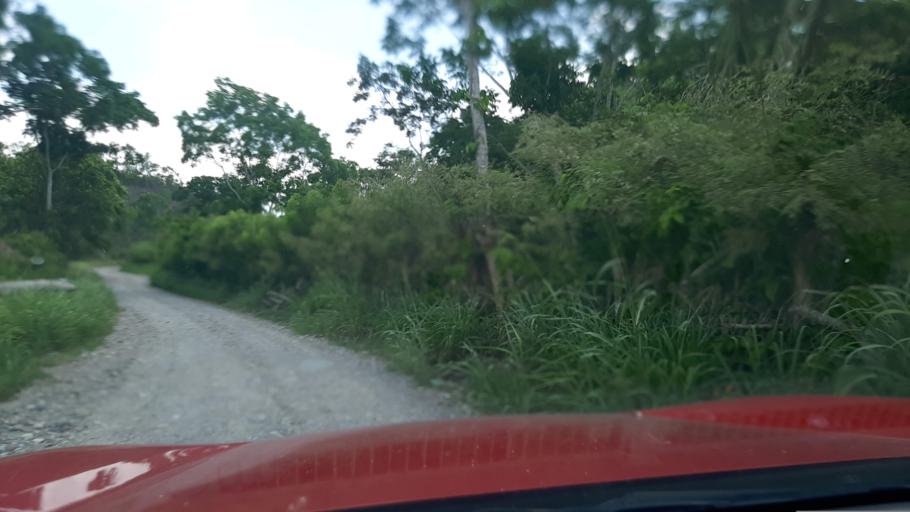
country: MX
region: Veracruz
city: Papantla de Olarte
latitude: 20.4178
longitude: -97.2778
